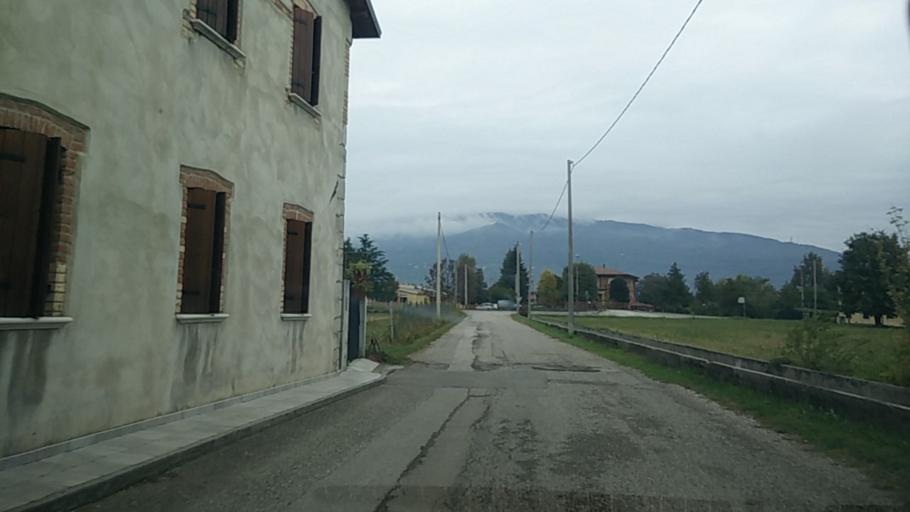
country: IT
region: Veneto
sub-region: Provincia di Treviso
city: Godega
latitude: 45.9514
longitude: 12.3873
